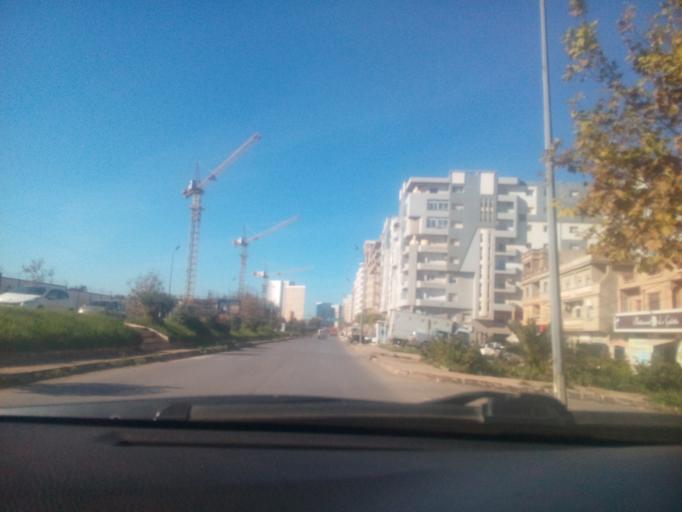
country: DZ
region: Oran
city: Bir el Djir
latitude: 35.7169
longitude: -0.5935
